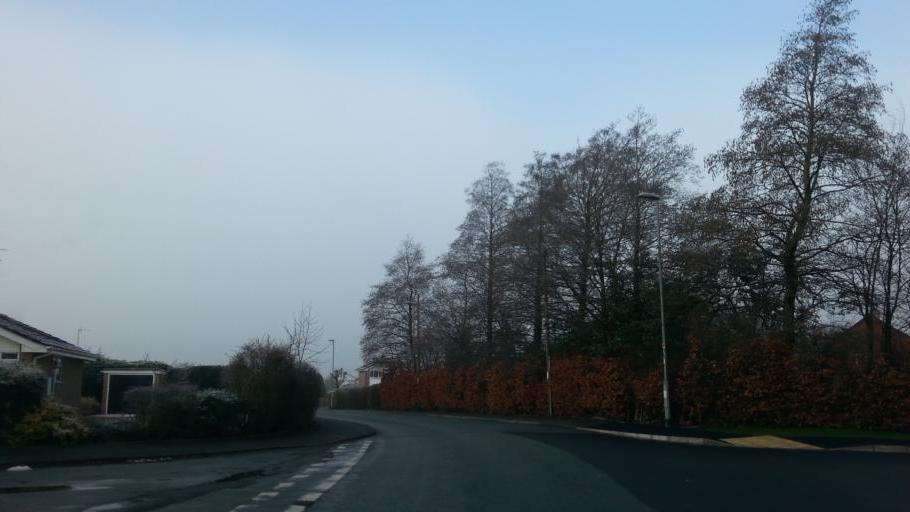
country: GB
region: England
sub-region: Staffordshire
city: Biddulph
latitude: 53.1213
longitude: -2.1636
